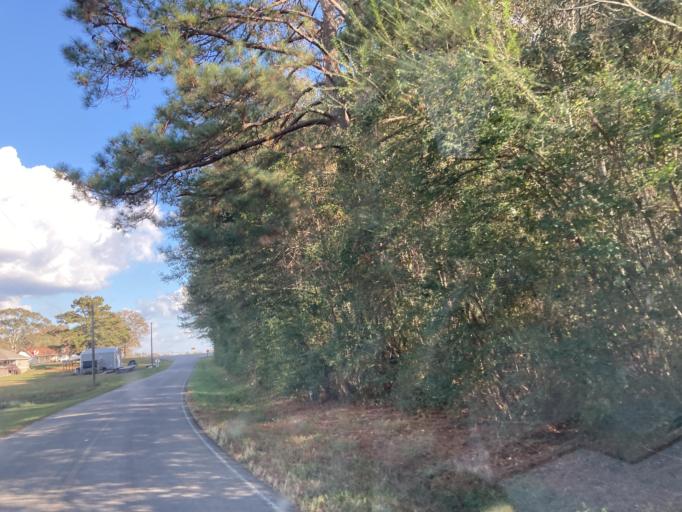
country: US
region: Mississippi
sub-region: Lamar County
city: Sumrall
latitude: 31.4268
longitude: -89.6418
